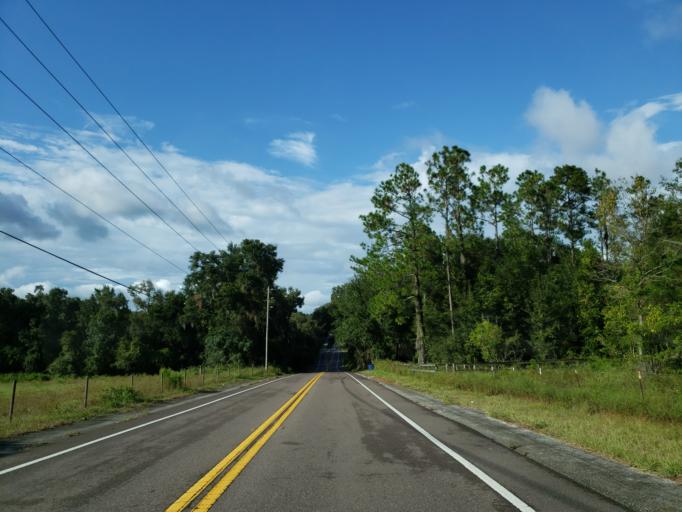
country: US
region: Florida
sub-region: Hernando County
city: Hill 'n Dale
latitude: 28.4488
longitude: -82.3029
